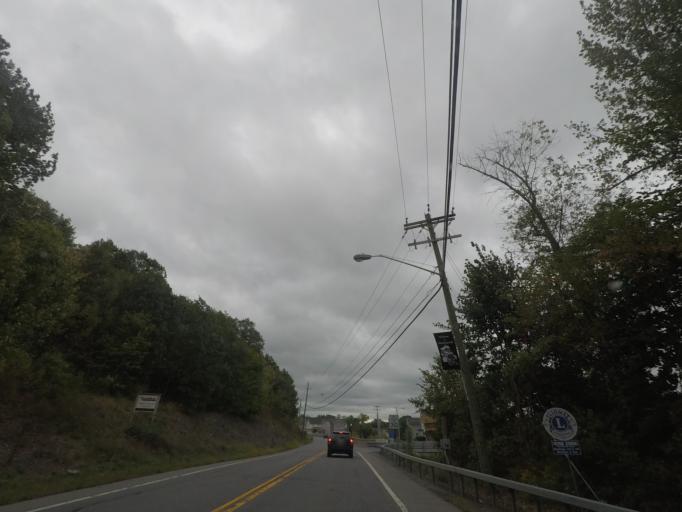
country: US
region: New York
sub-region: Saratoga County
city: Mechanicville
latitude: 42.9121
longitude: -73.6989
